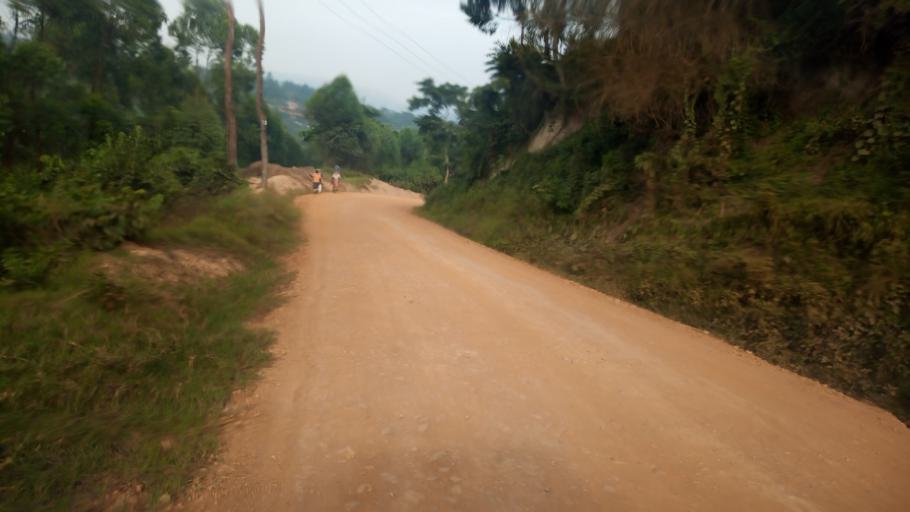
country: UG
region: Western Region
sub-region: Kanungu District
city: Ntungamo
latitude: -0.8388
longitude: 29.6466
